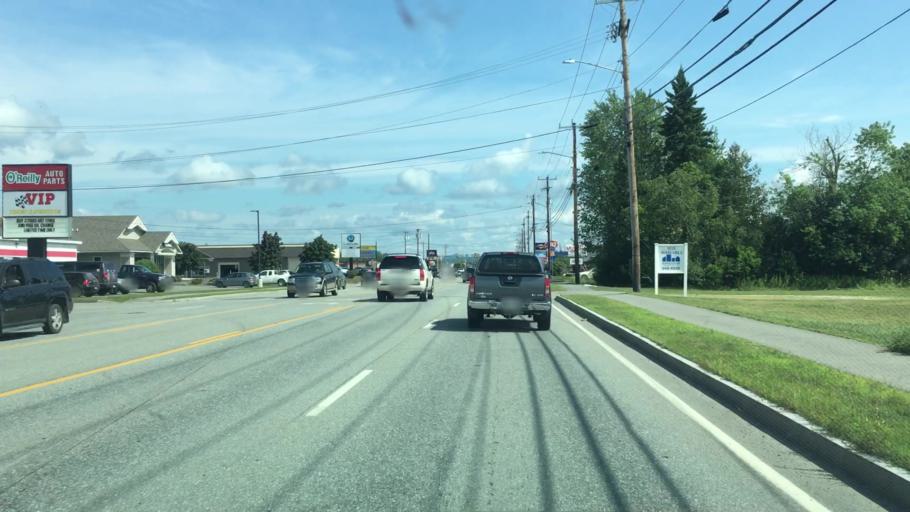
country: US
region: Maine
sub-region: Penobscot County
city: Brewer
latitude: 44.7818
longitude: -68.7461
